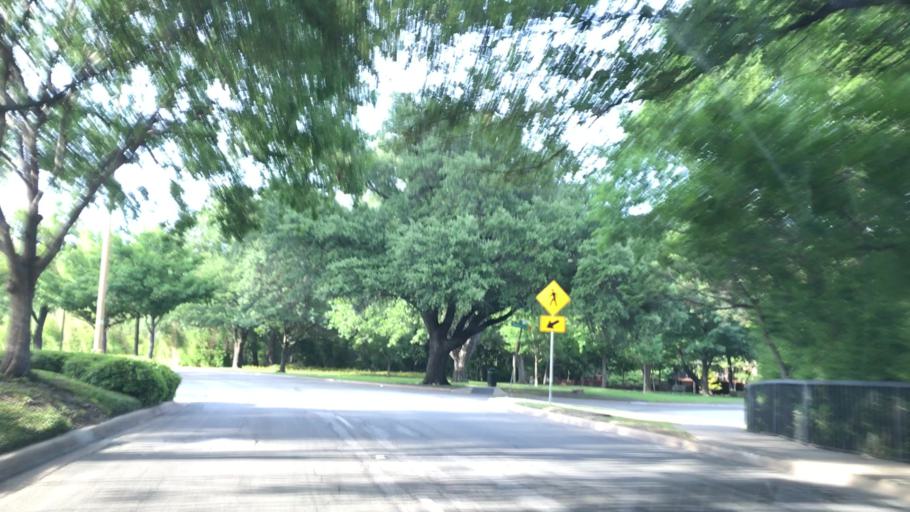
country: US
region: Texas
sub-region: Dallas County
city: Highland Park
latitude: 32.8148
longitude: -96.7987
